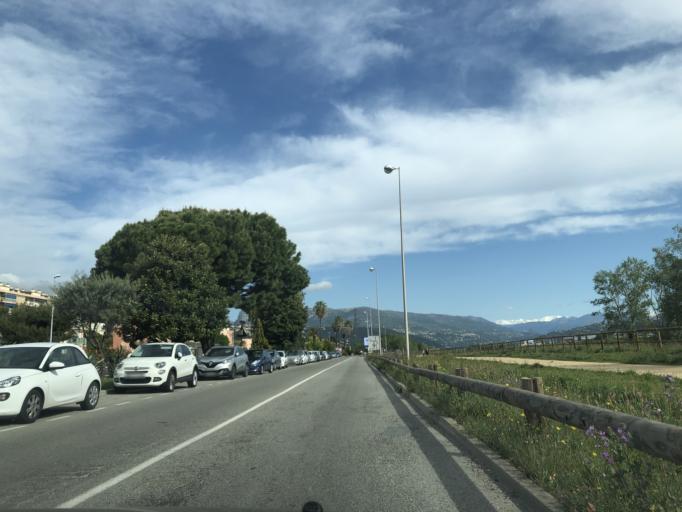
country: FR
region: Provence-Alpes-Cote d'Azur
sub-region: Departement des Alpes-Maritimes
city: Saint-Laurent-du-Var
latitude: 43.6808
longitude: 7.1900
